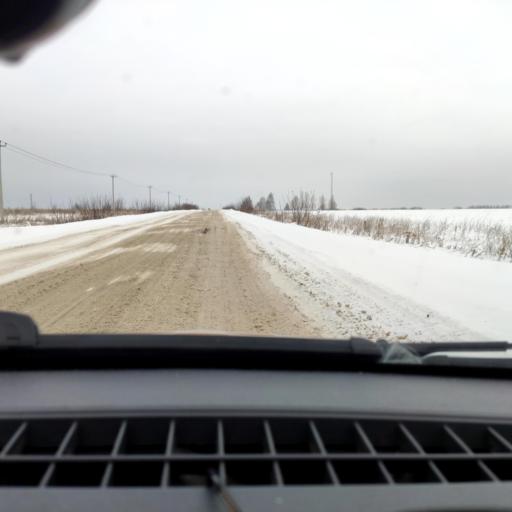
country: RU
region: Bashkortostan
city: Iglino
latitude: 54.8459
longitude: 56.4021
